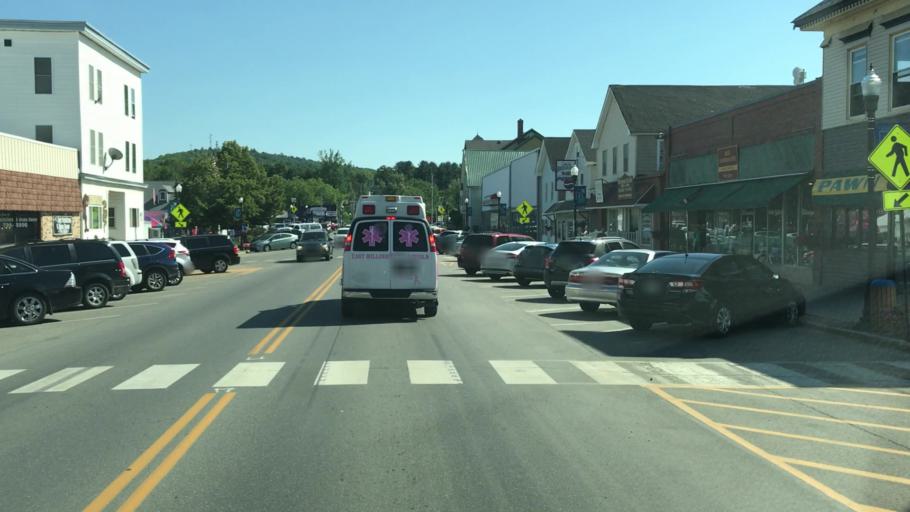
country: US
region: Maine
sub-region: Penobscot County
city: Lincoln
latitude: 45.3639
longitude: -68.5039
